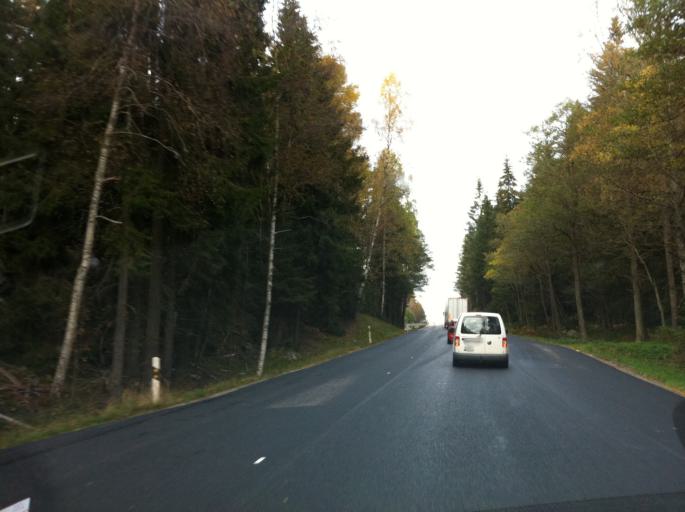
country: SE
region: OEstergoetland
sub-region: Motala Kommun
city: Ryd
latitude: 58.7588
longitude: 14.9915
